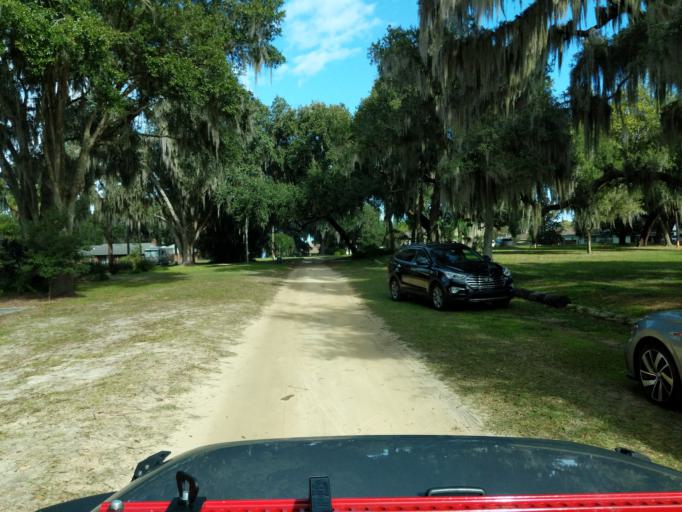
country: US
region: Florida
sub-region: Orange County
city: Oakland
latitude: 28.5587
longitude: -81.6305
